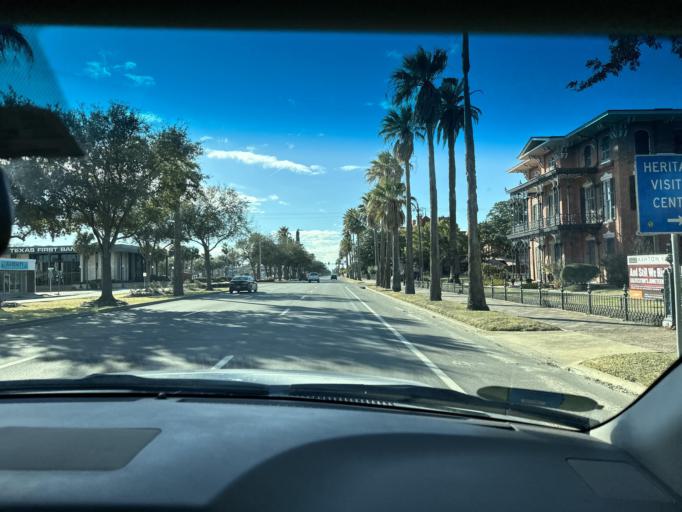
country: US
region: Texas
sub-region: Galveston County
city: Galveston
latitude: 29.3001
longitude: -94.7924
